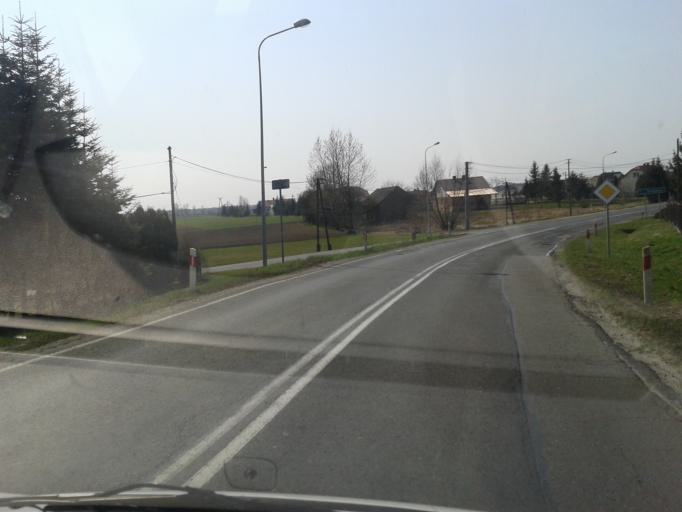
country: PL
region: Subcarpathian Voivodeship
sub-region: Powiat jaroslawski
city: Laszki
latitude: 50.0778
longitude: 22.8513
